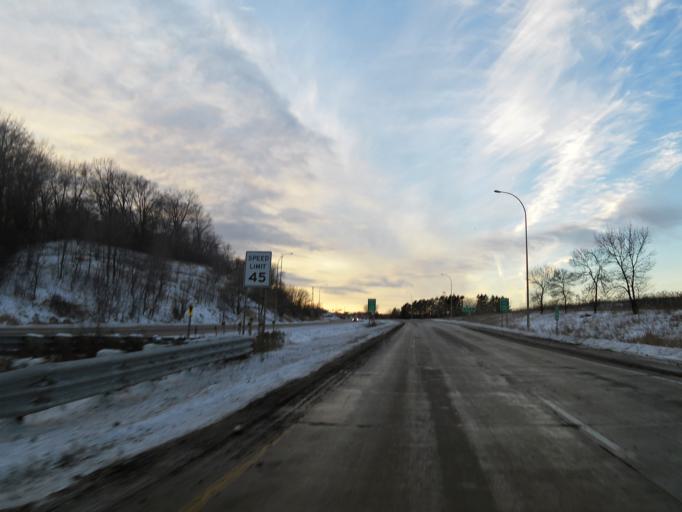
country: US
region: Minnesota
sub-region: Hennepin County
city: Hopkins
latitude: 44.8921
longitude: -93.4344
